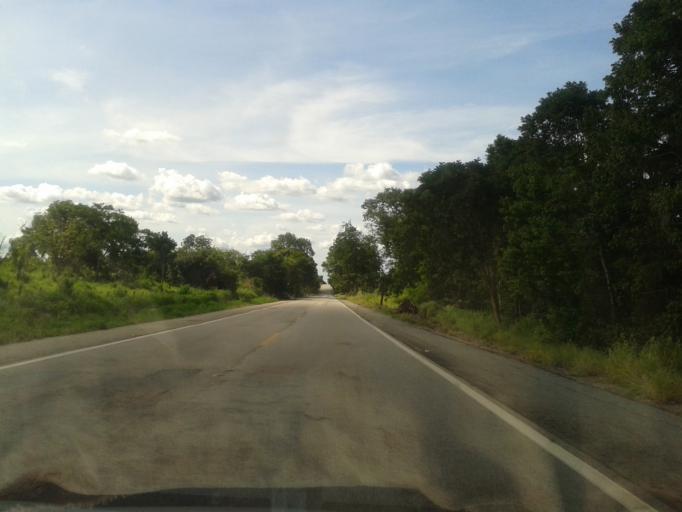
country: BR
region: Goias
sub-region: Mozarlandia
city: Mozarlandia
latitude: -15.2379
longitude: -50.5138
